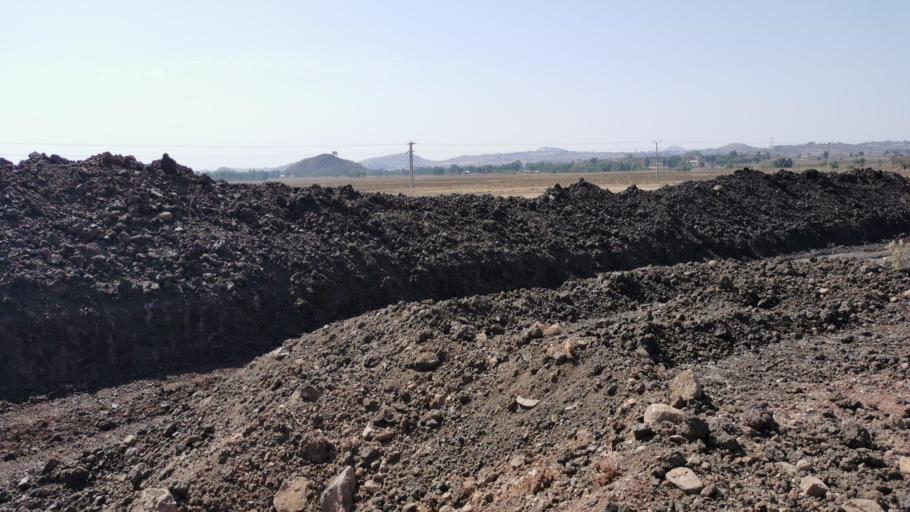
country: ET
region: Amhara
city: Bahir Dar
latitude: 11.8389
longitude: 37.0016
